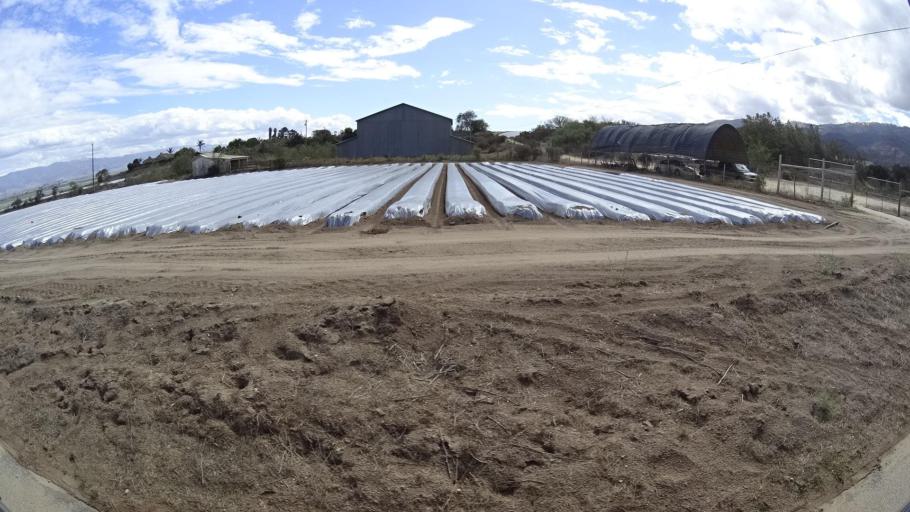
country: US
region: California
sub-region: Monterey County
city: Chualar
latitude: 36.5876
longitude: -121.6077
